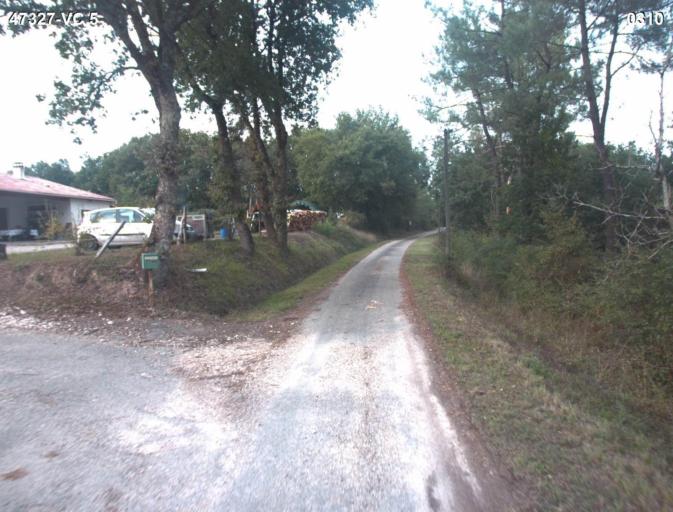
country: FR
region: Aquitaine
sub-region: Departement du Lot-et-Garonne
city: Buzet-sur-Baise
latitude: 44.2197
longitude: 0.2726
